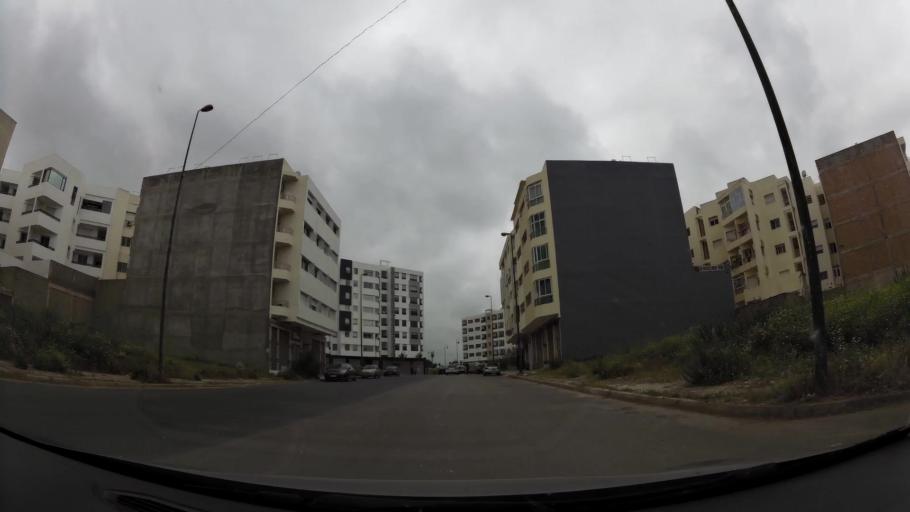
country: MA
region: Fes-Boulemane
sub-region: Fes
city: Fes
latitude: 34.0374
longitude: -5.0149
